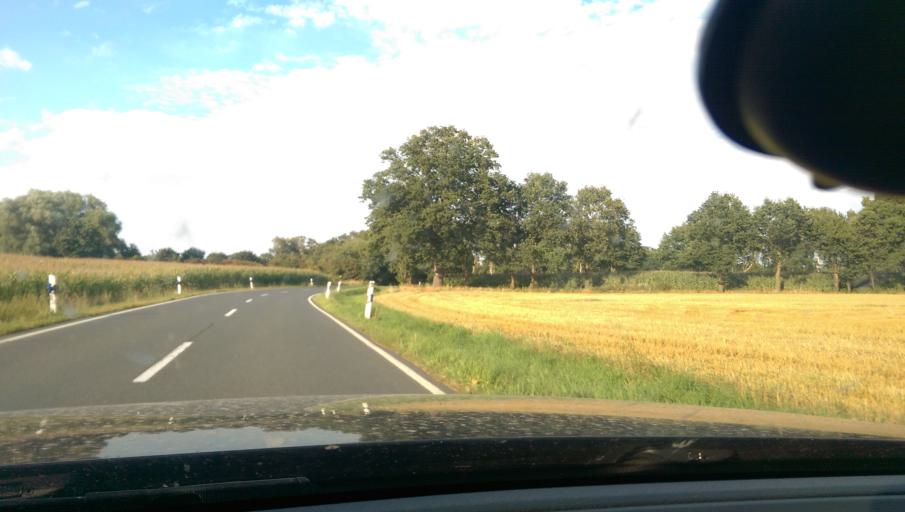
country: DE
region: Lower Saxony
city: Neustadt am Rubenberge
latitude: 52.5710
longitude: 9.5585
